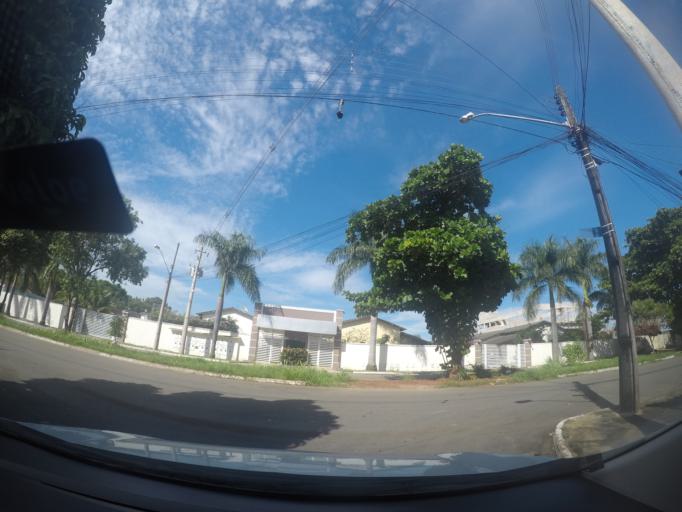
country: BR
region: Goias
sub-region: Goiania
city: Goiania
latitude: -16.6605
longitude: -49.2068
